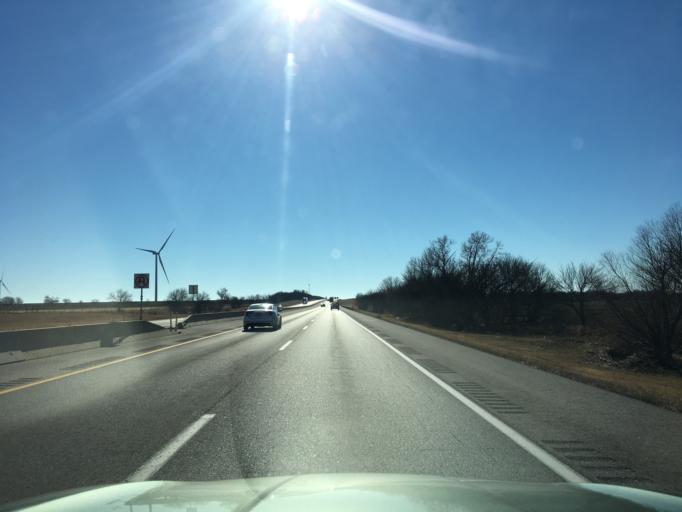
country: US
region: Kansas
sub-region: Sumner County
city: Wellington
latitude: 37.1359
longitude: -97.3392
